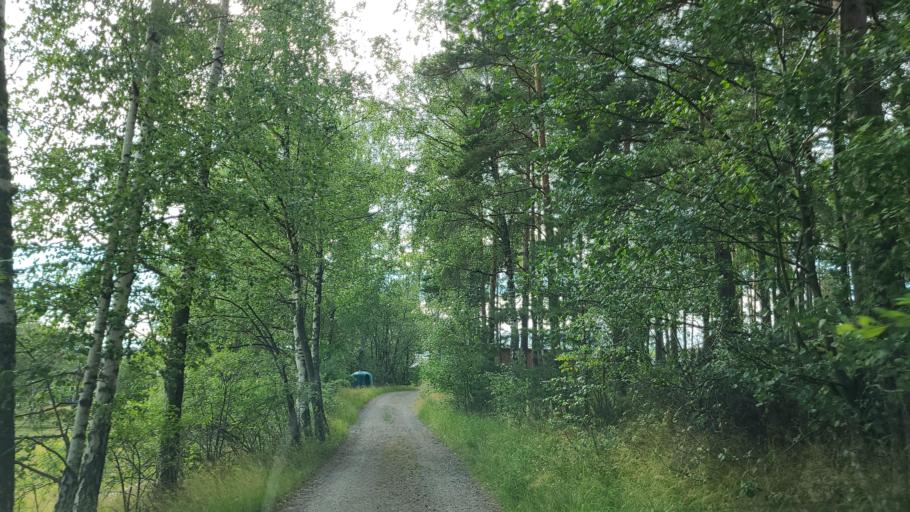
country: FI
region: Varsinais-Suomi
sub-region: Turku
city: Rymaettylae
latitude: 60.2807
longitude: 21.9516
